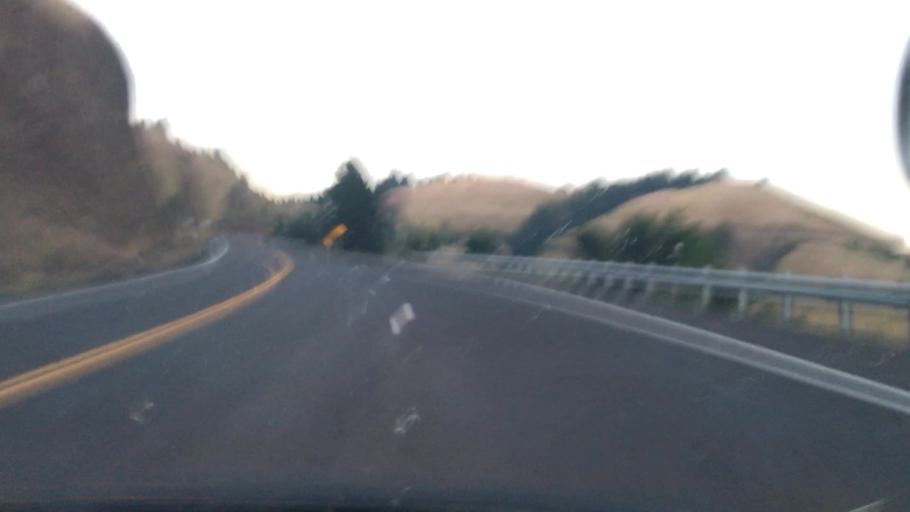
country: US
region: Idaho
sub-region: Idaho County
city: Grangeville
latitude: 45.8335
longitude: -116.2405
